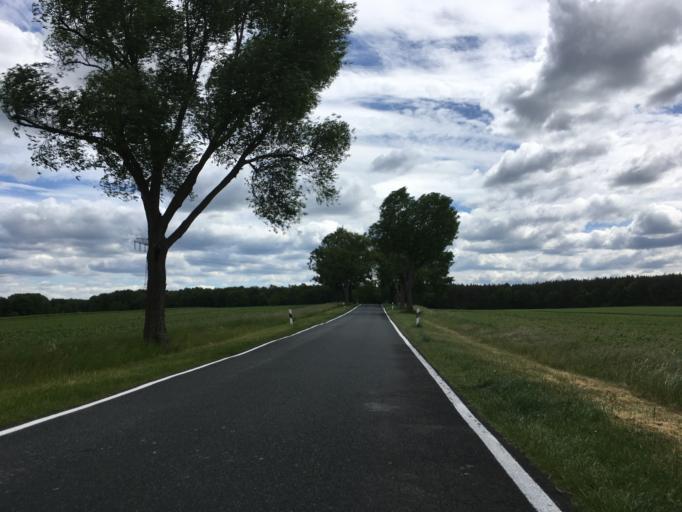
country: DE
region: Brandenburg
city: Melchow
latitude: 52.7393
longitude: 13.7328
